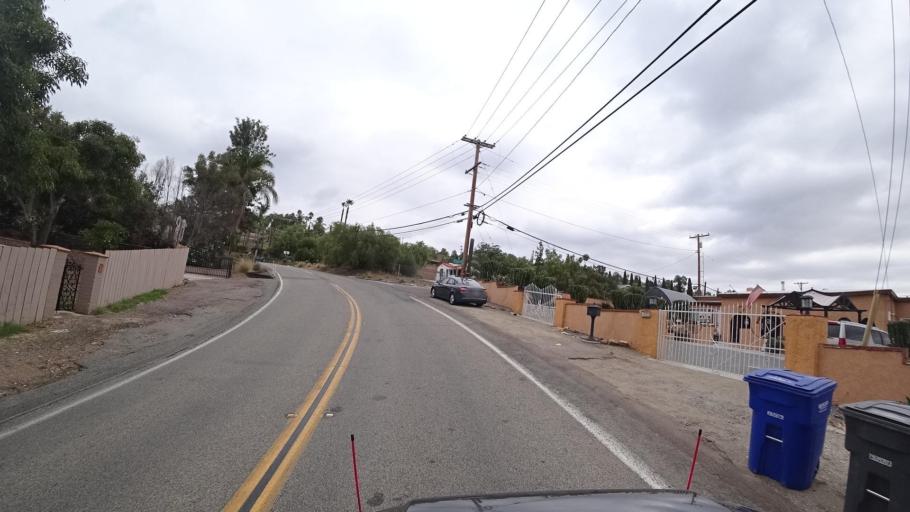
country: US
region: California
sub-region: San Diego County
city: Spring Valley
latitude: 32.7536
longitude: -116.9859
